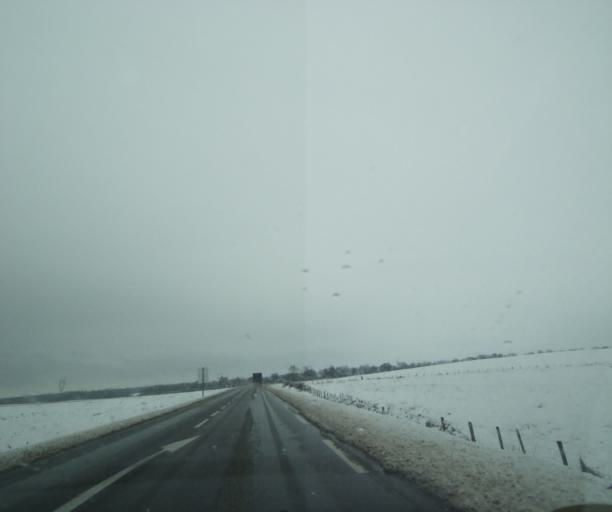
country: FR
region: Champagne-Ardenne
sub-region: Departement de la Haute-Marne
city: Montier-en-Der
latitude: 48.5127
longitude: 4.8042
